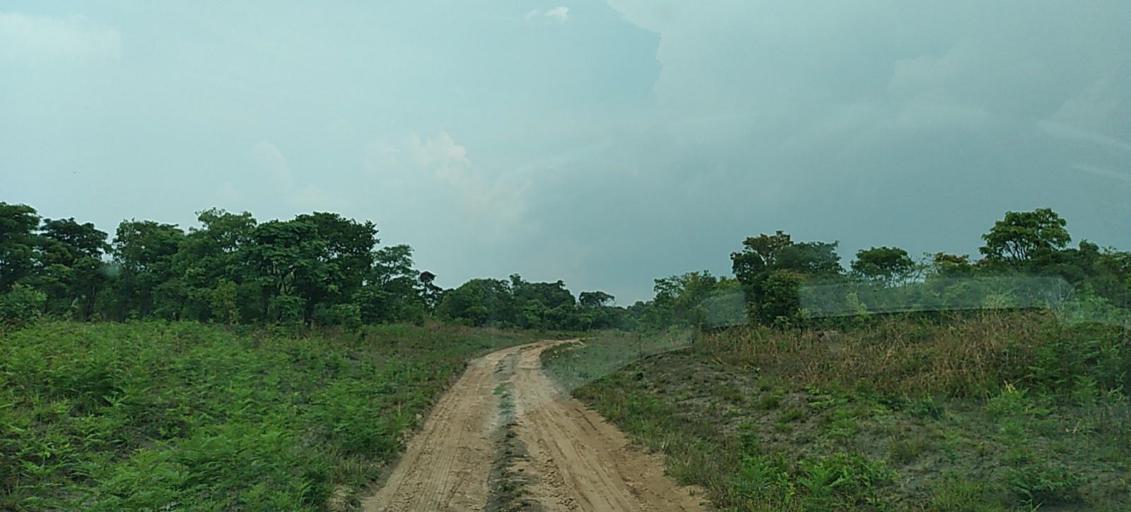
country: ZM
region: North-Western
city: Mwinilunga
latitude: -11.4329
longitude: 24.5937
